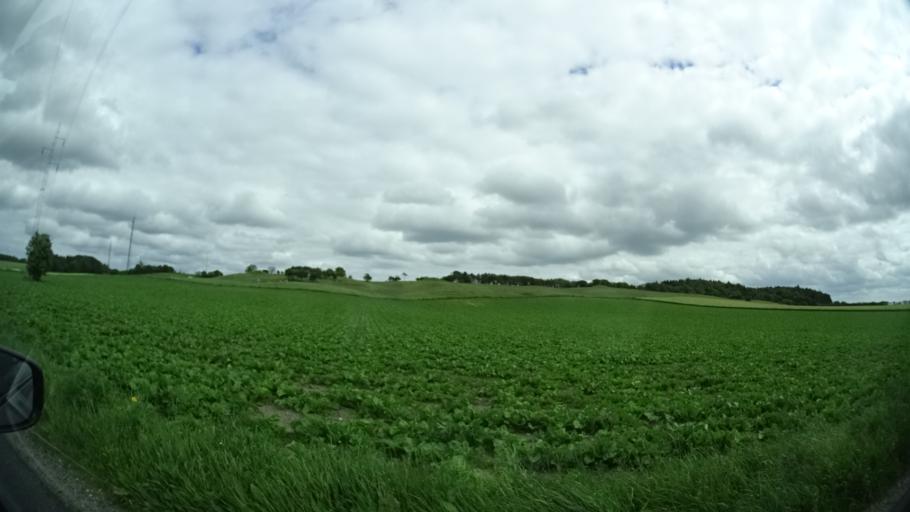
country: DK
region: Central Jutland
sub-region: Norddjurs Kommune
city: Grenaa
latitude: 56.4687
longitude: 10.7153
